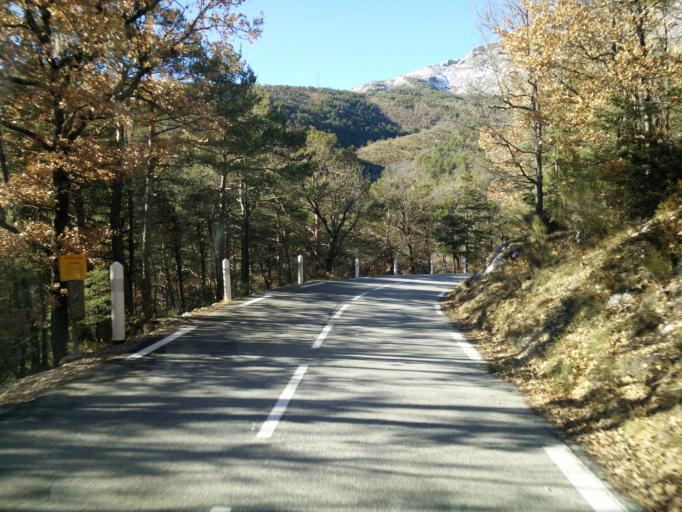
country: FR
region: Provence-Alpes-Cote d'Azur
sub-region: Departement des Alpes-de-Haute-Provence
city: Castellane
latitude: 43.8002
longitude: 6.4406
